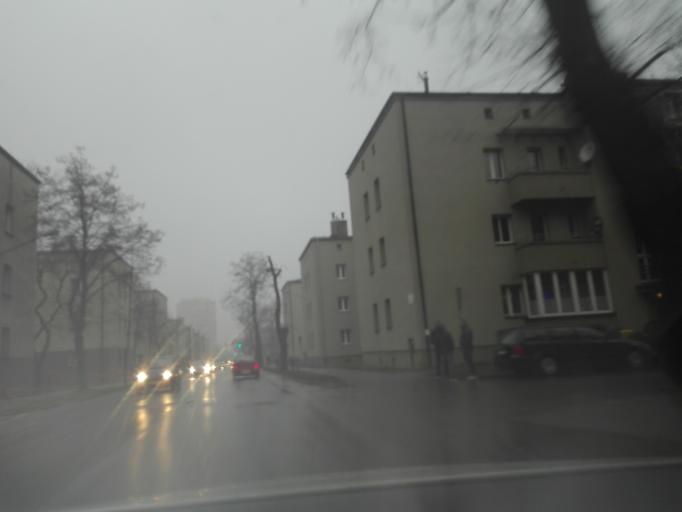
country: PL
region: Silesian Voivodeship
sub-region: Katowice
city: Katowice
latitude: 50.2689
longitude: 19.0313
